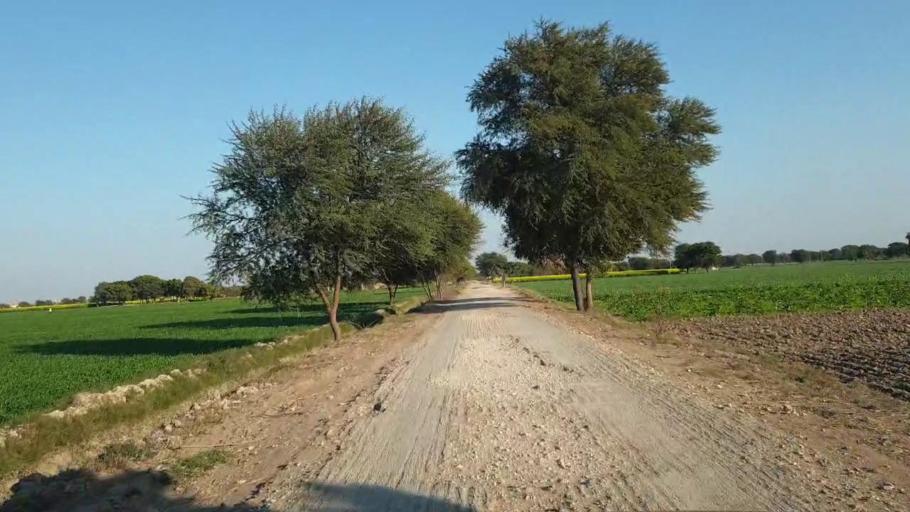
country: PK
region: Sindh
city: Shahpur Chakar
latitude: 26.1274
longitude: 68.5549
